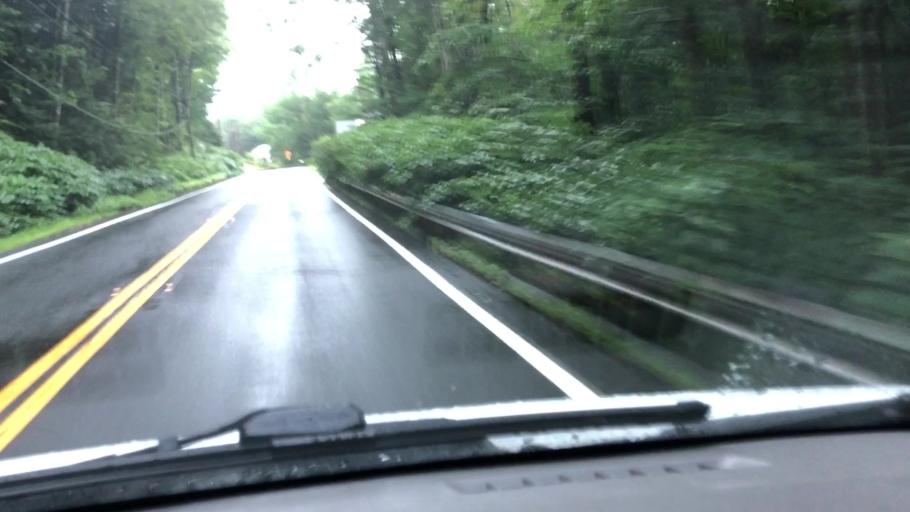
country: US
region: Massachusetts
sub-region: Hampshire County
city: Chesterfield
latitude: 42.3414
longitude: -72.8881
